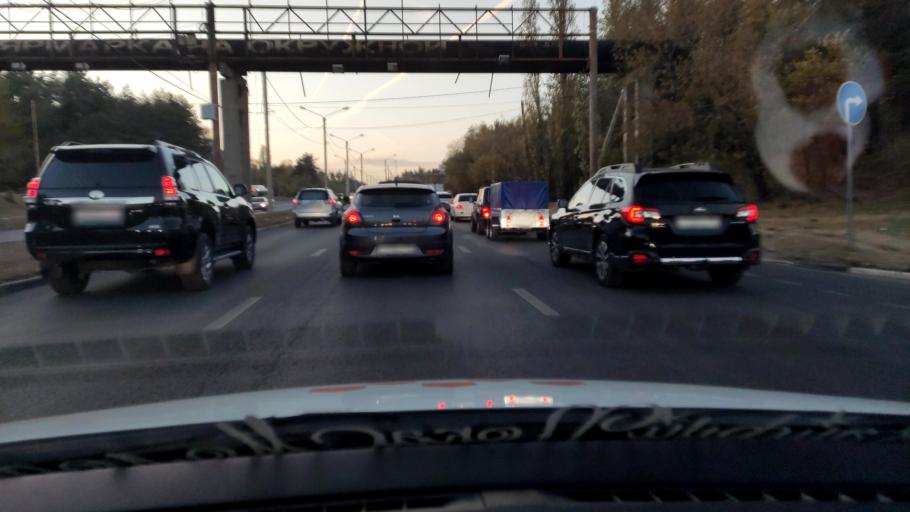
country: RU
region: Voronezj
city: Pridonskoy
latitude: 51.6724
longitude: 39.1197
